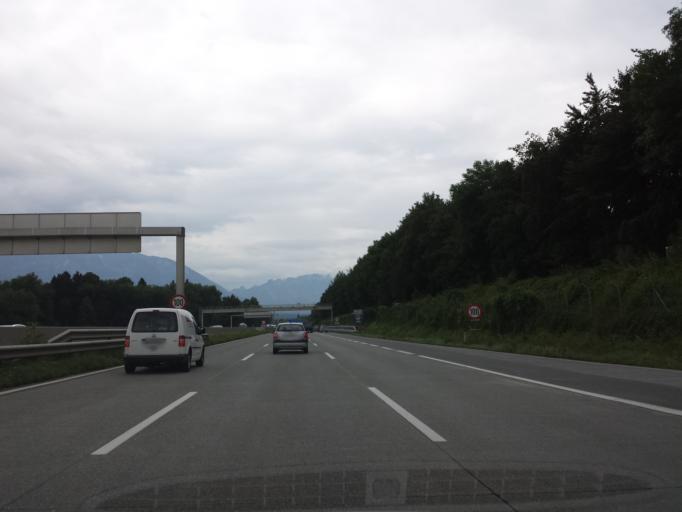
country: DE
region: Bavaria
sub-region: Upper Bavaria
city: Freilassing
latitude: 47.8032
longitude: 12.9910
